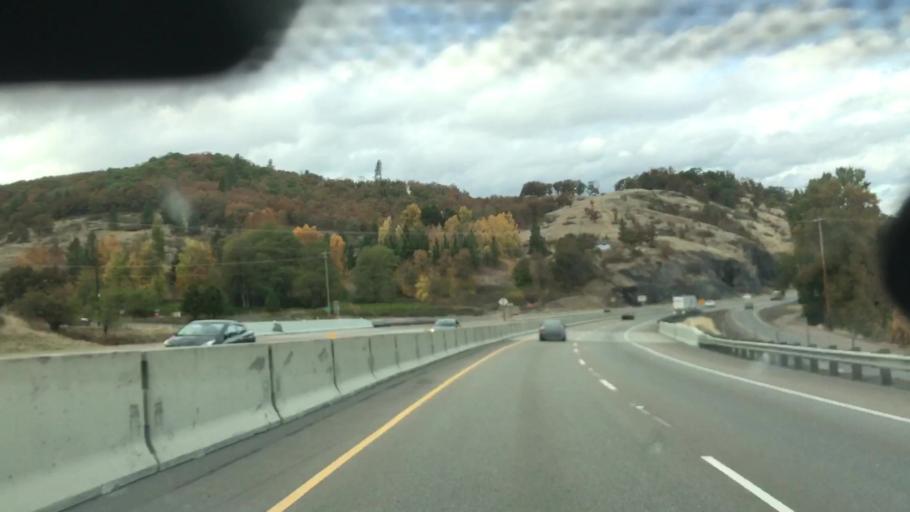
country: US
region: Oregon
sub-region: Douglas County
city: Green
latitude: 43.1829
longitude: -123.3740
